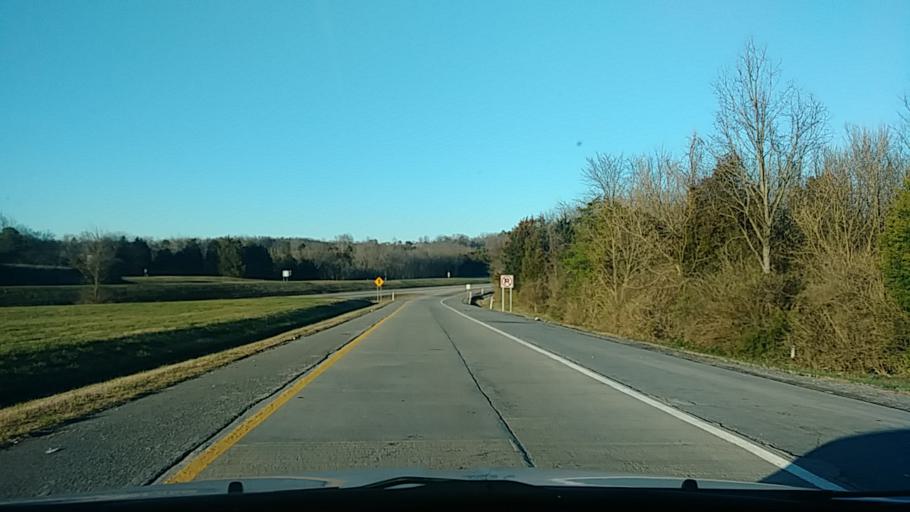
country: US
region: Tennessee
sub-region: Hamblen County
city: Morristown
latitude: 36.1675
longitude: -83.2178
